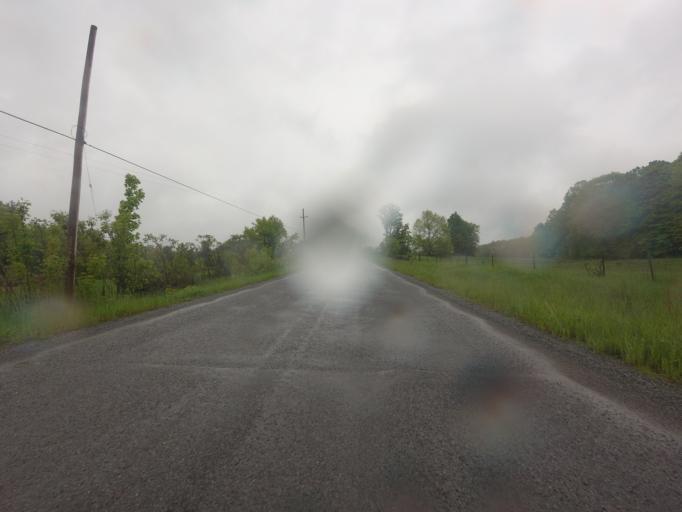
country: CA
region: Ontario
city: Kingston
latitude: 44.4894
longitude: -76.4393
